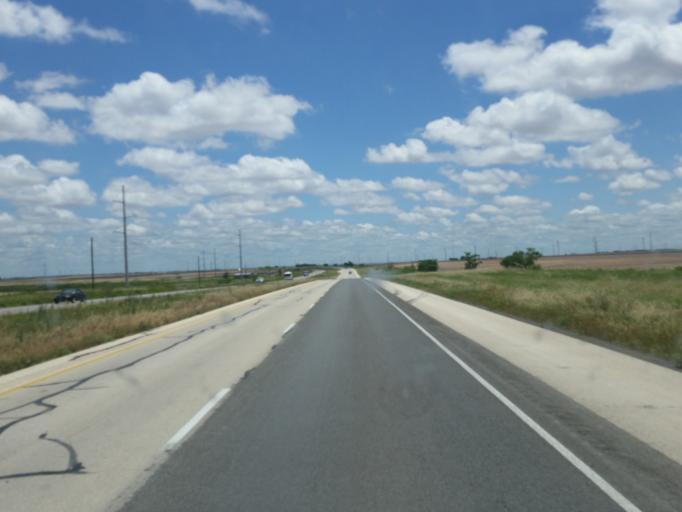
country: US
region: Texas
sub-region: Nolan County
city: Roscoe
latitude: 32.4962
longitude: -100.6374
